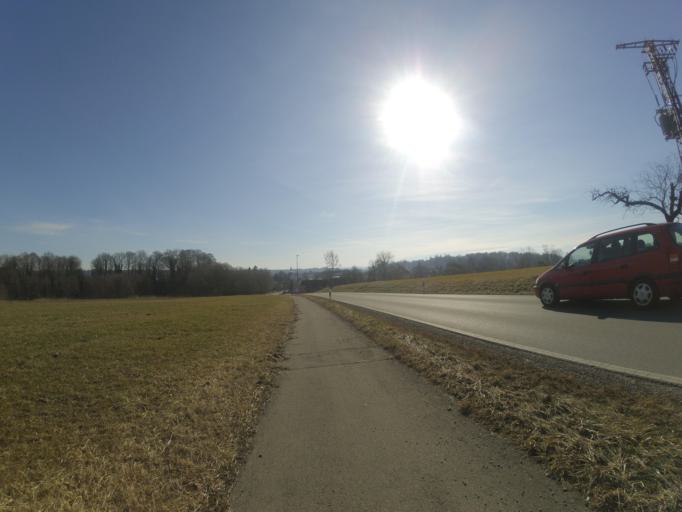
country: DE
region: Baden-Wuerttemberg
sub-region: Tuebingen Region
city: Wolpertswende
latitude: 47.8796
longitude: 9.6213
